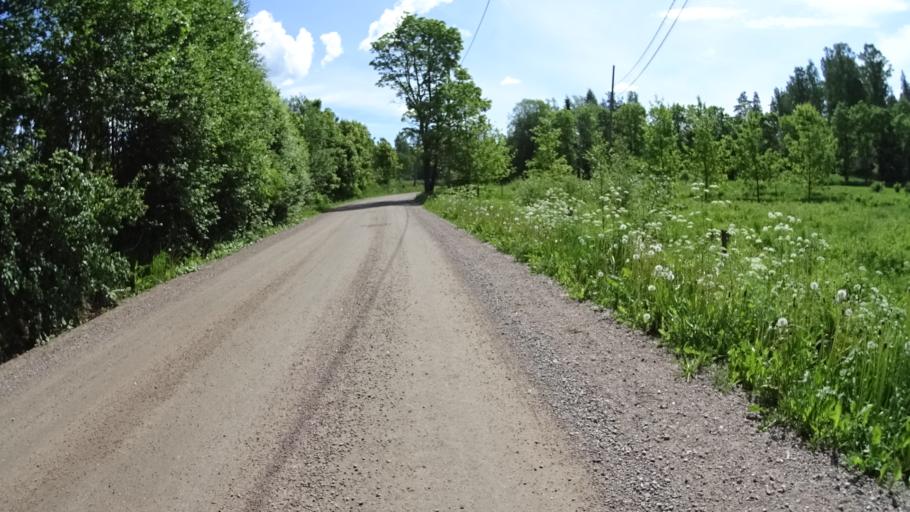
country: FI
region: Uusimaa
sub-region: Helsinki
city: Kauniainen
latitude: 60.2975
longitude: 24.6842
